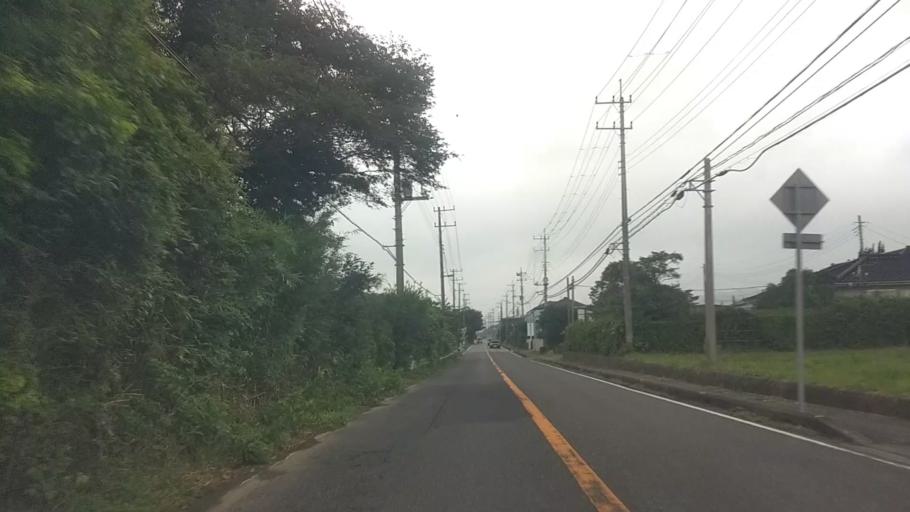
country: JP
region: Chiba
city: Kawaguchi
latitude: 35.1223
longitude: 140.0651
